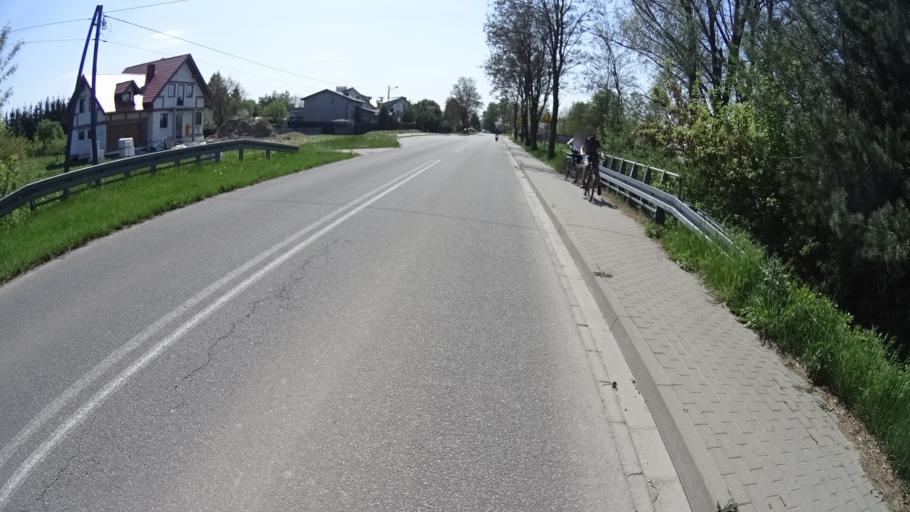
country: PL
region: Masovian Voivodeship
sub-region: Powiat warszawski zachodni
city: Jozefow
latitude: 52.2612
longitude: 20.6986
